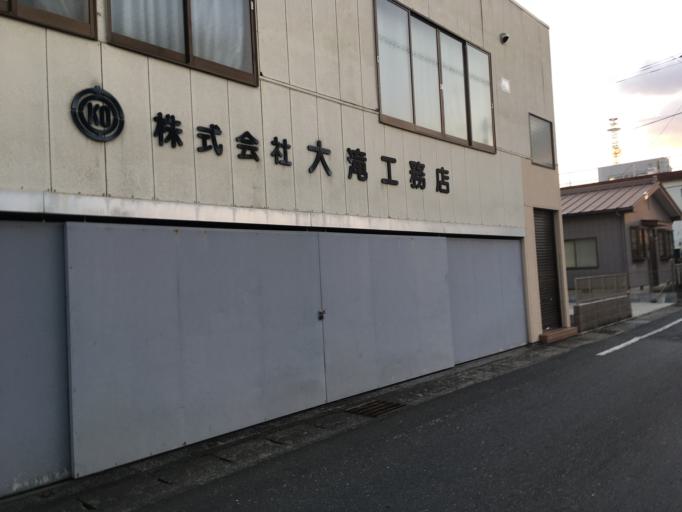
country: JP
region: Chiba
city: Tateyama
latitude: 34.9934
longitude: 139.8594
